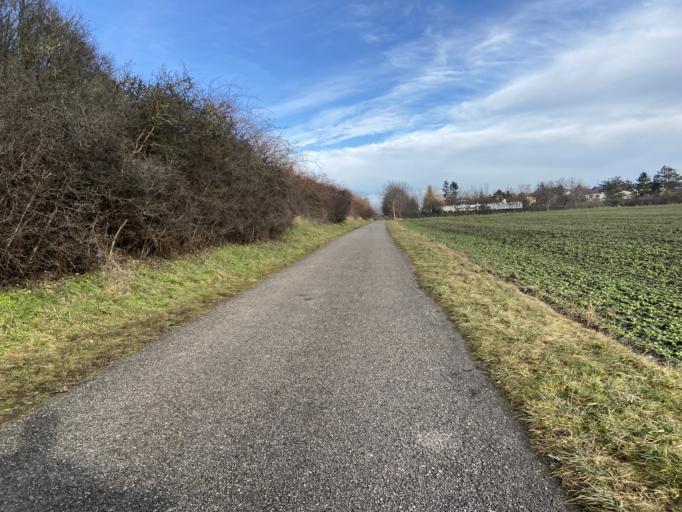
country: AT
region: Lower Austria
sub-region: Politischer Bezirk Modling
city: Laxenburg
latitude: 48.0681
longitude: 16.3451
